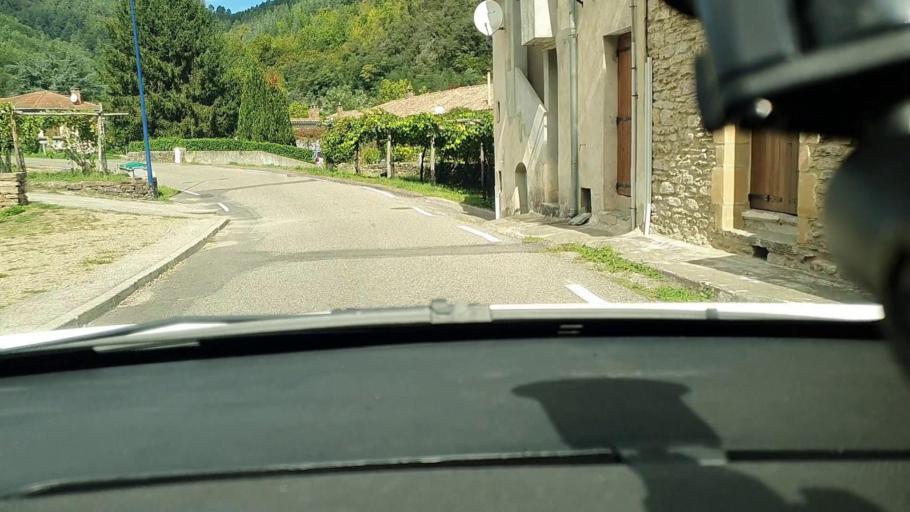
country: FR
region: Languedoc-Roussillon
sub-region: Departement du Gard
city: Besseges
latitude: 44.3008
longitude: 4.0182
